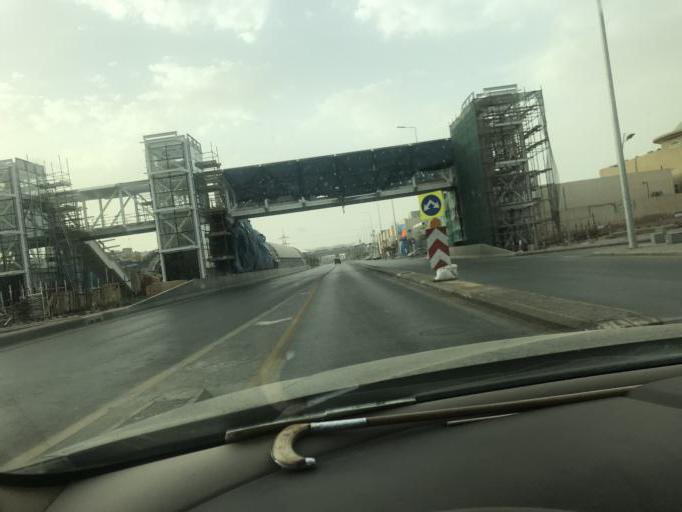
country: SA
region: Ar Riyad
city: Riyadh
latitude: 24.7786
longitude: 46.6642
